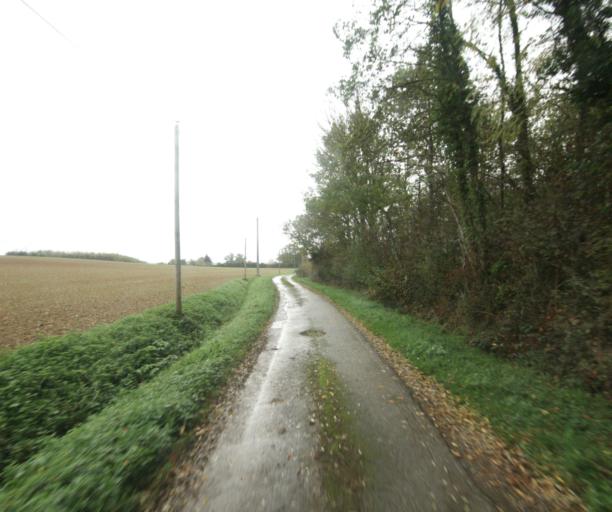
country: FR
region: Rhone-Alpes
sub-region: Departement de l'Ain
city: Pont-de-Vaux
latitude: 46.4851
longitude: 4.8806
